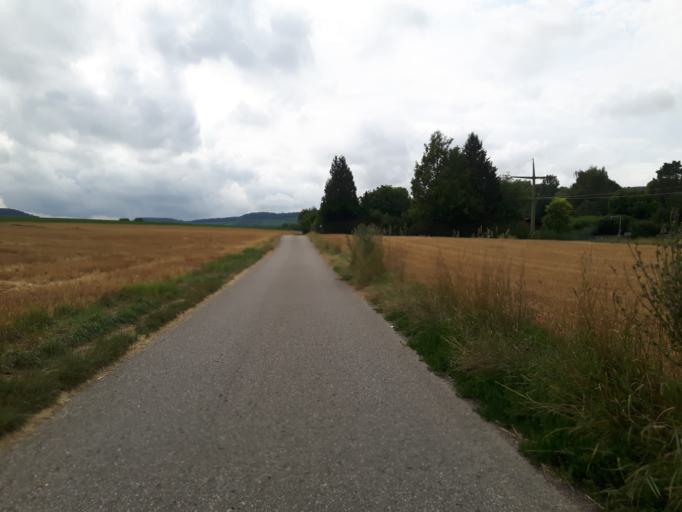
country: DE
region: Baden-Wuerttemberg
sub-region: Regierungsbezirk Stuttgart
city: Nordheim
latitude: 49.1108
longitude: 9.1168
